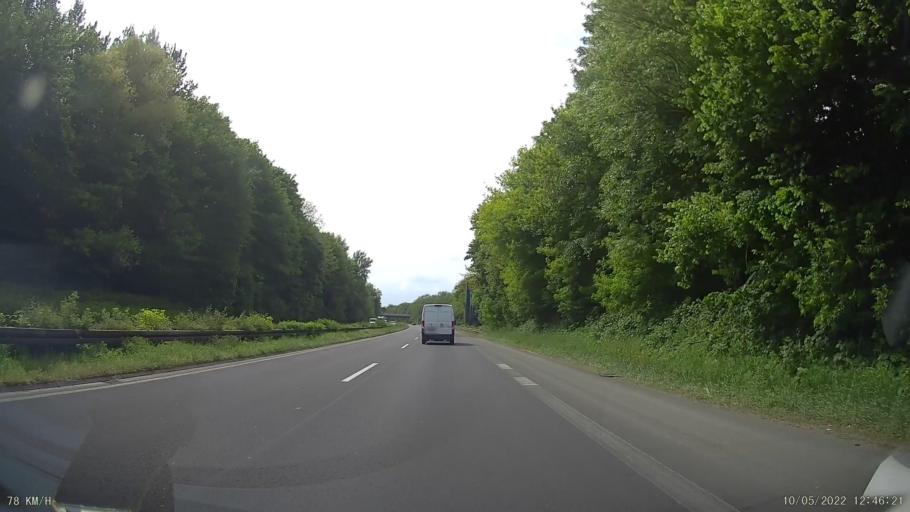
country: DE
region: North Rhine-Westphalia
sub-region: Regierungsbezirk Arnsberg
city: Dortmund
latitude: 51.5232
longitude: 7.4022
